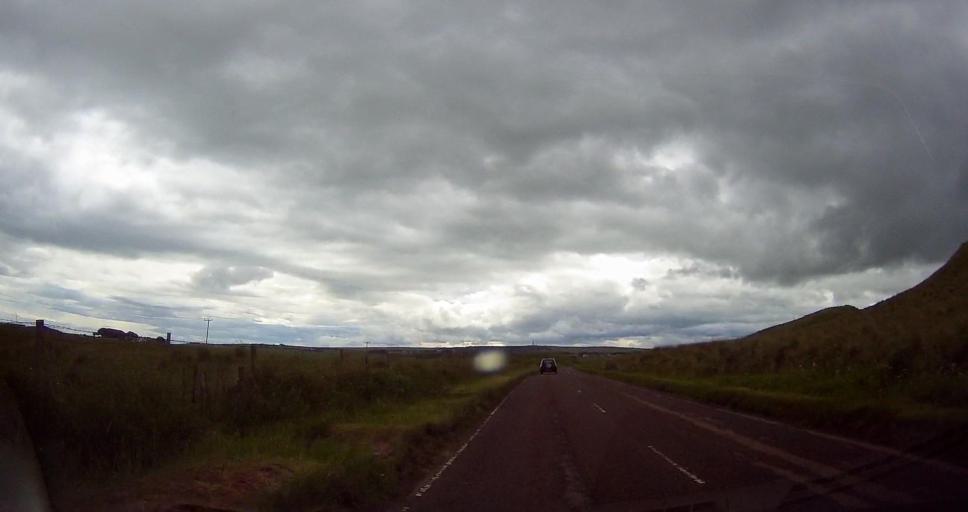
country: GB
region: Scotland
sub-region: Highland
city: Thurso
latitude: 58.5964
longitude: -3.3570
